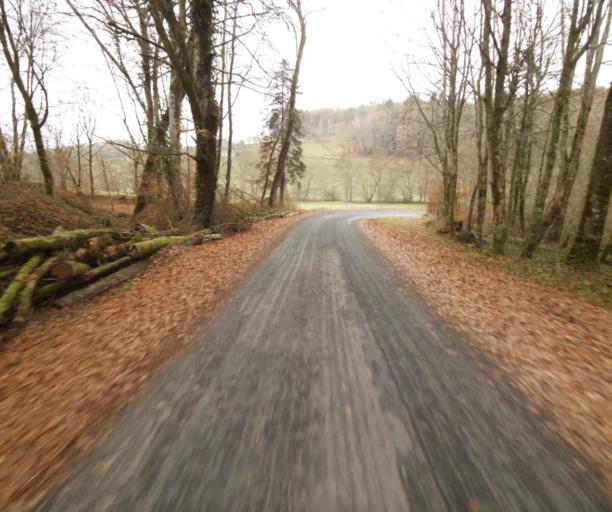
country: FR
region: Limousin
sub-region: Departement de la Correze
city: Sainte-Fortunade
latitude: 45.2241
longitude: 1.7494
